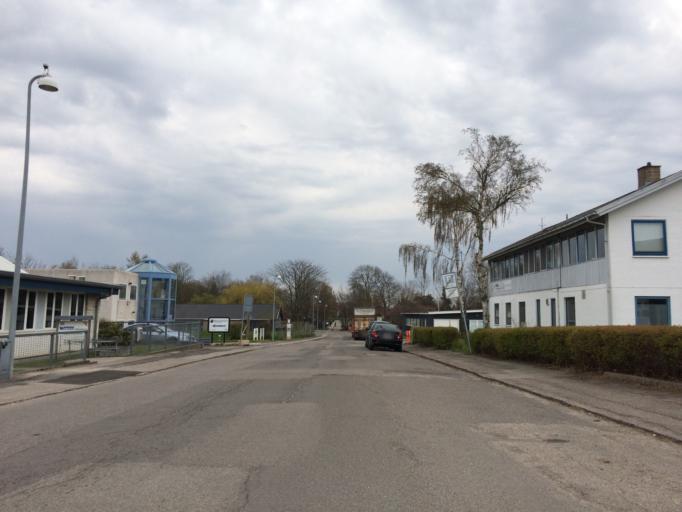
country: DK
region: Capital Region
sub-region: Hoje-Taastrup Kommune
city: Taastrup
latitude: 55.6498
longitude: 12.2897
